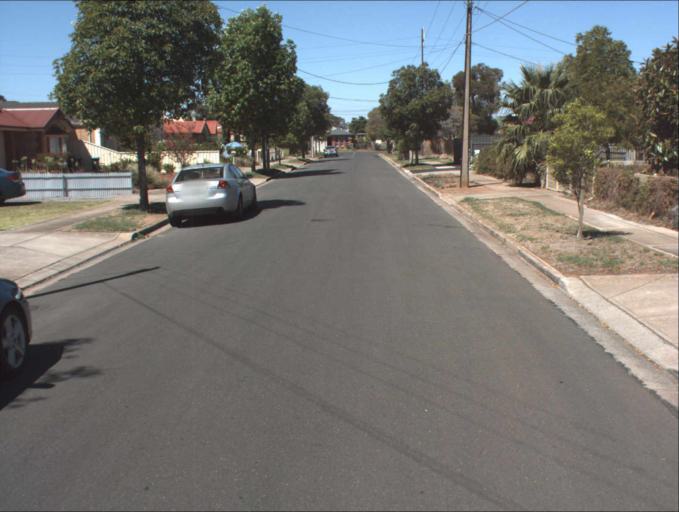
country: AU
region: South Australia
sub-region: Port Adelaide Enfield
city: Enfield
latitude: -34.8595
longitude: 138.6155
